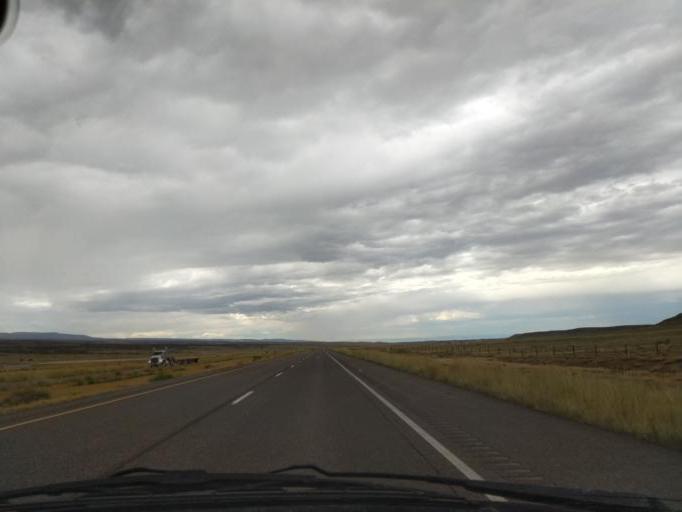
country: US
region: Colorado
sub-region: Mesa County
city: Palisade
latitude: 38.8764
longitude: -108.3458
